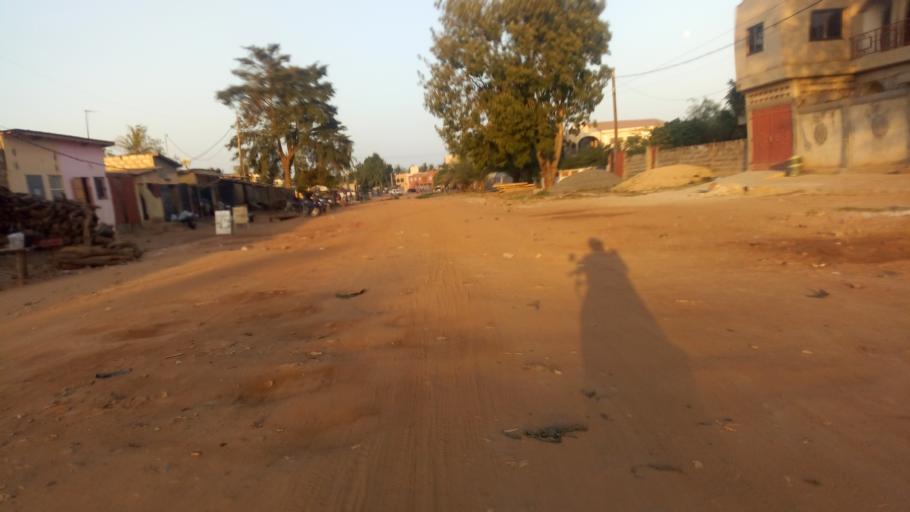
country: TG
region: Maritime
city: Lome
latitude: 6.1927
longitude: 1.1958
